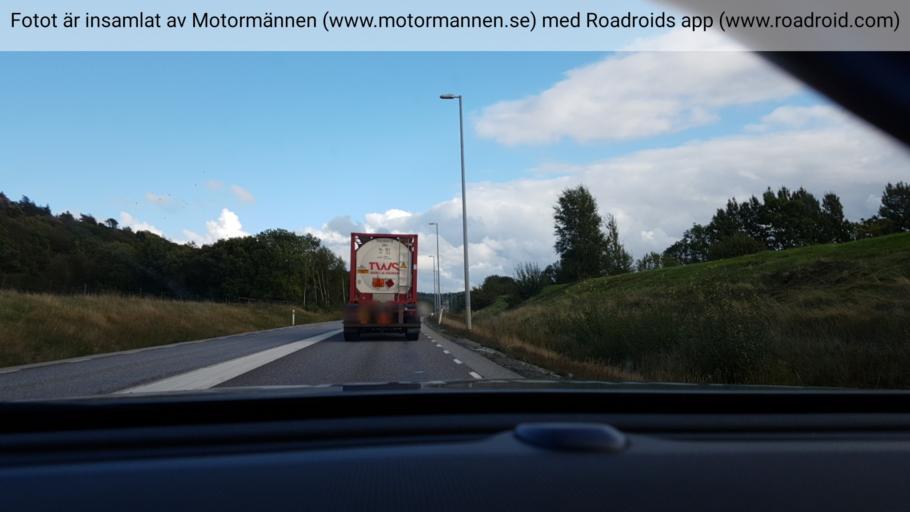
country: SE
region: Vaestra Goetaland
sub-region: Stenungsunds Kommun
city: Stenungsund
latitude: 58.0689
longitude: 11.8576
